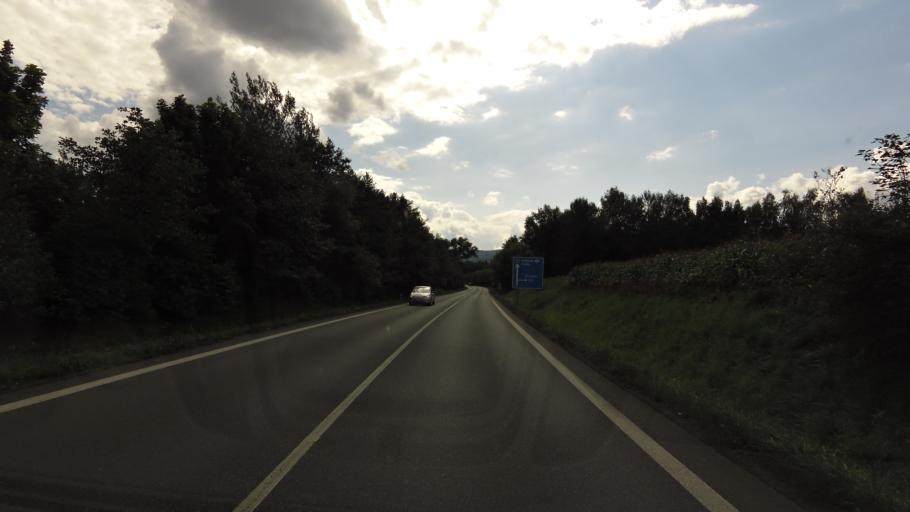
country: CZ
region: Plzensky
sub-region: Okres Domazlice
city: Domazlice
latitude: 49.4221
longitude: 12.8779
